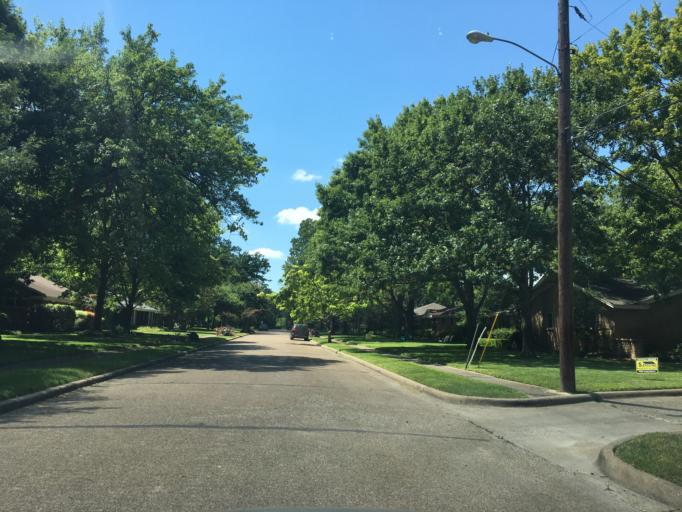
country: US
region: Texas
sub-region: Dallas County
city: Garland
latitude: 32.8467
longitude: -96.7001
